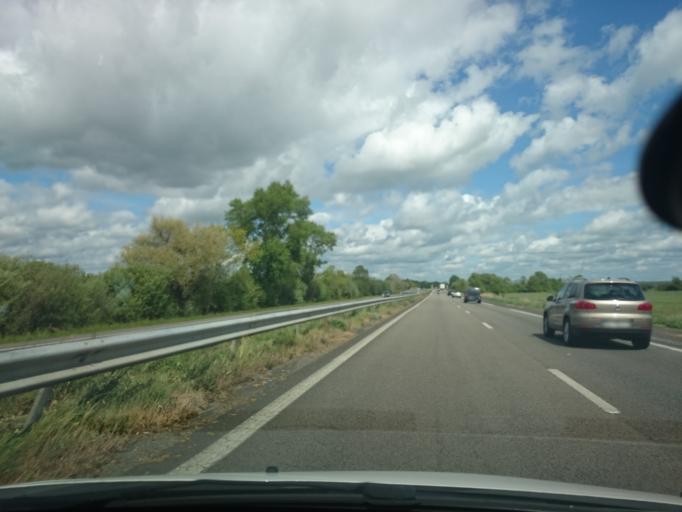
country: FR
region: Pays de la Loire
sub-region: Departement de la Loire-Atlantique
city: Donges
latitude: 47.3539
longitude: -2.0573
